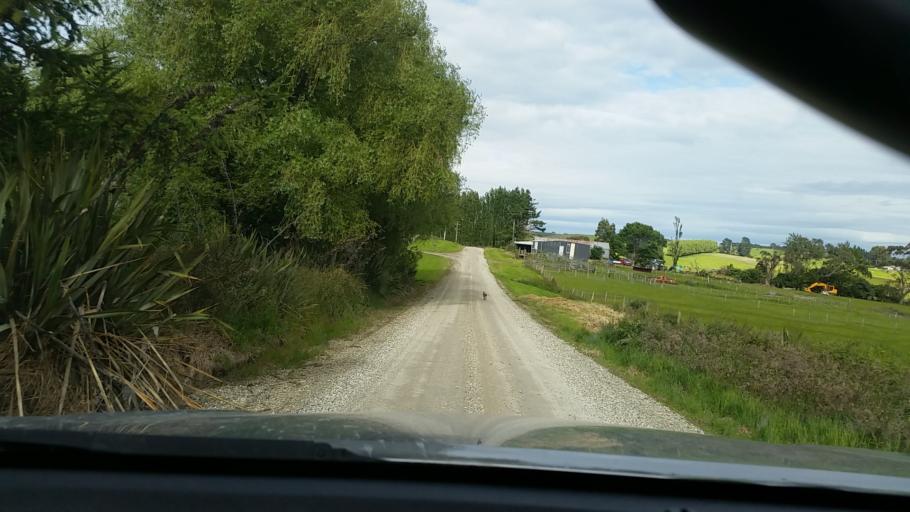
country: NZ
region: Southland
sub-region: Gore District
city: Gore
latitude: -46.2055
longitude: 168.7757
